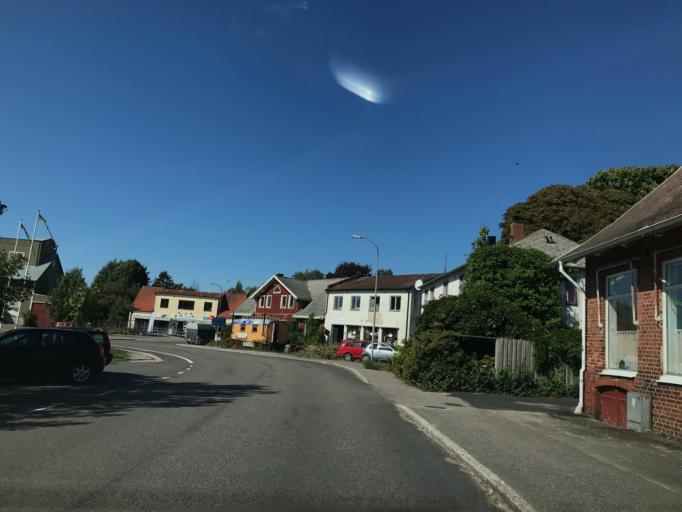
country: SE
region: Skane
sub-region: Tomelilla Kommun
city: Tomelilla
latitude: 55.6550
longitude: 13.8909
